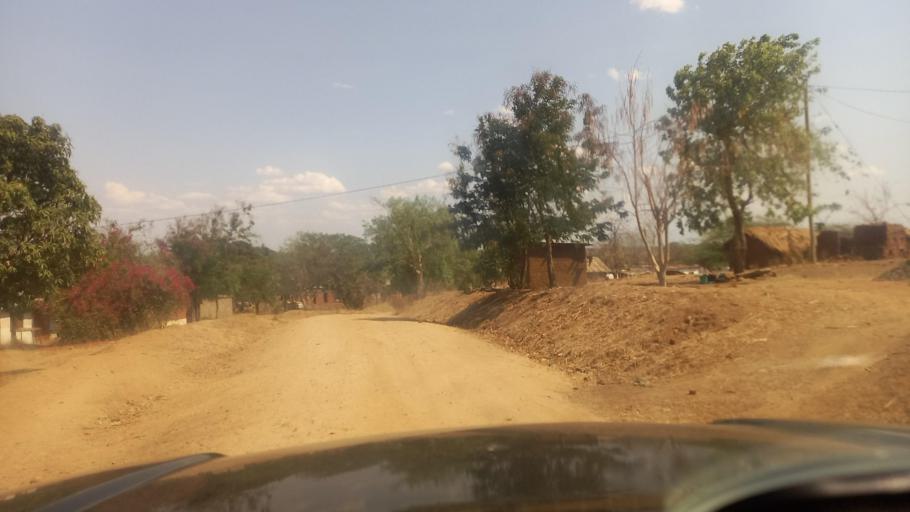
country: TZ
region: Morogoro
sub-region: Kilosa
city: Magole
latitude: -6.3206
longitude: 37.3725
